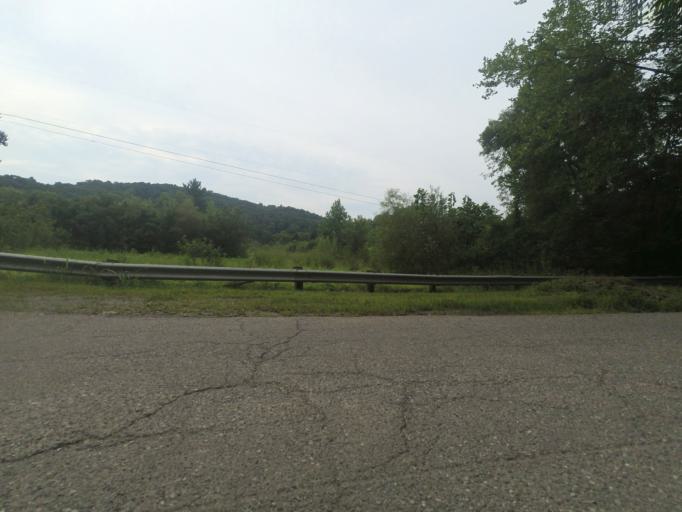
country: US
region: West Virginia
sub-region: Cabell County
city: Huntington
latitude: 38.4417
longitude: -82.4541
